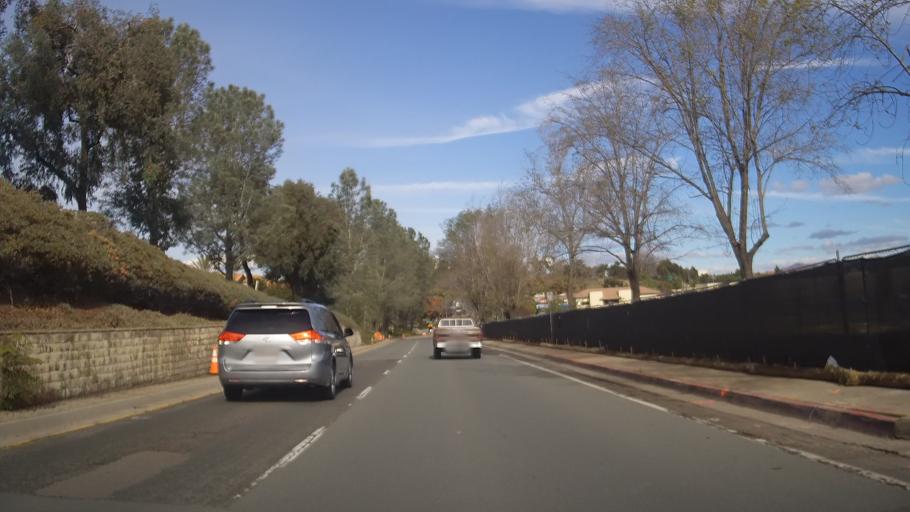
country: US
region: California
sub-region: San Diego County
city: Poway
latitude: 32.9750
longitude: -117.0918
